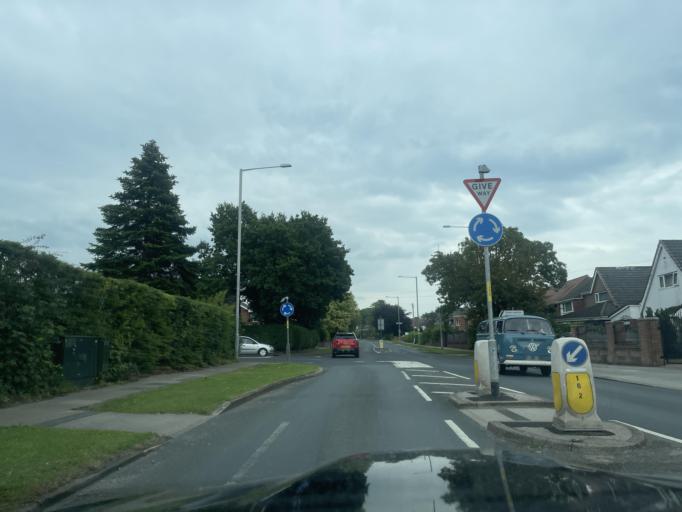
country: GB
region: England
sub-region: Lancashire
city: Leyland
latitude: 53.6884
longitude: -2.7115
